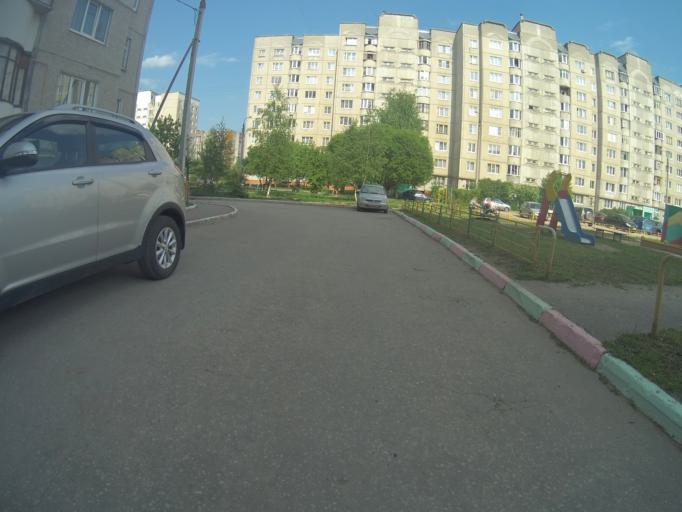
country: RU
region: Vladimir
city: Kommunar
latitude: 56.1673
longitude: 40.4515
